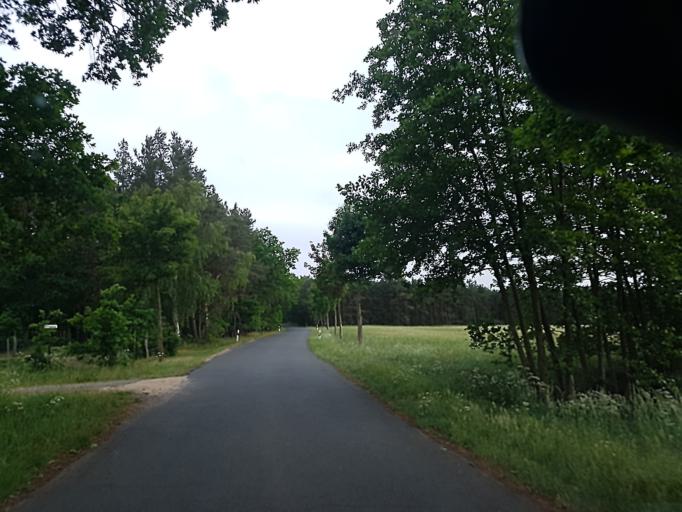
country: DE
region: Saxony-Anhalt
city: Holzdorf
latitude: 51.7743
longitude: 13.1122
